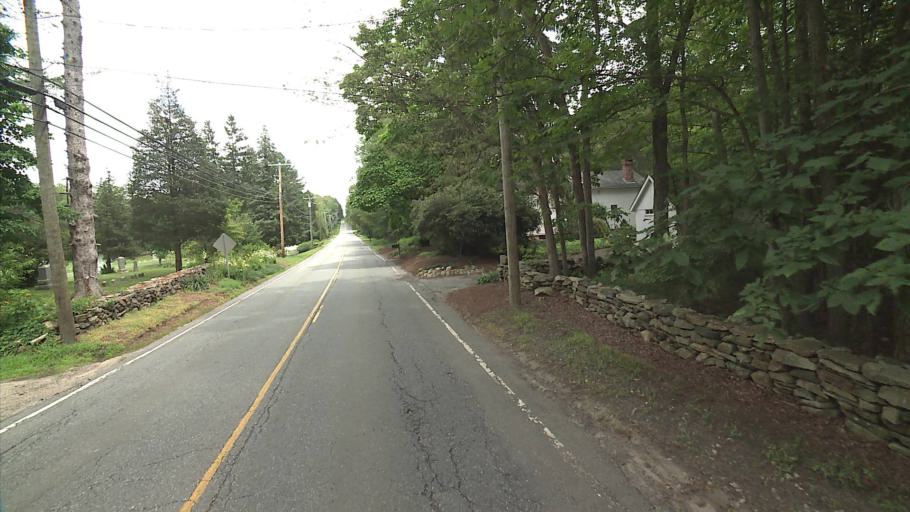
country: US
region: Connecticut
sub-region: Middlesex County
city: Chester Center
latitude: 41.3627
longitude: -72.4870
